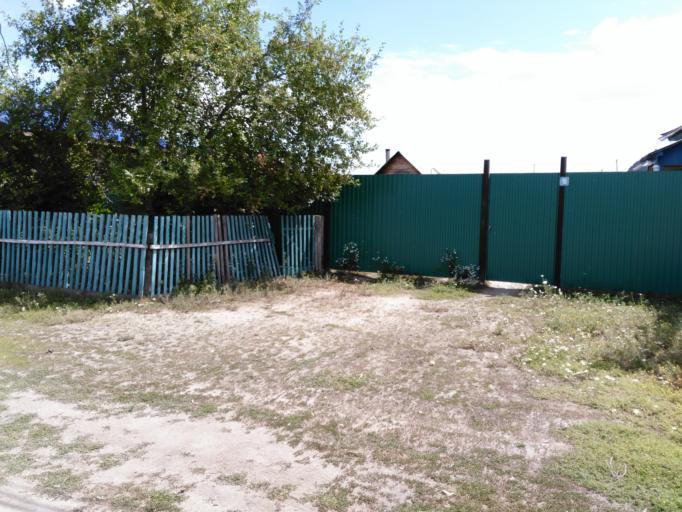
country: RU
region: Bashkortostan
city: Akhunovo
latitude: 54.2066
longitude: 59.5968
